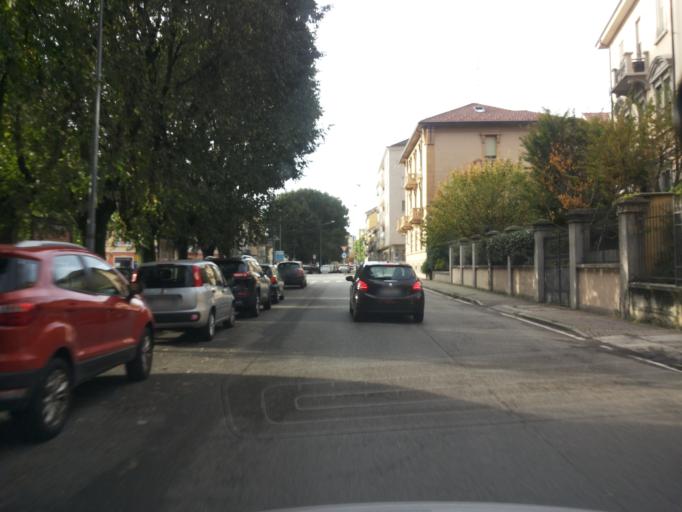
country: IT
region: Piedmont
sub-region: Provincia di Alessandria
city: Casale Monferrato
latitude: 45.1310
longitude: 8.4528
